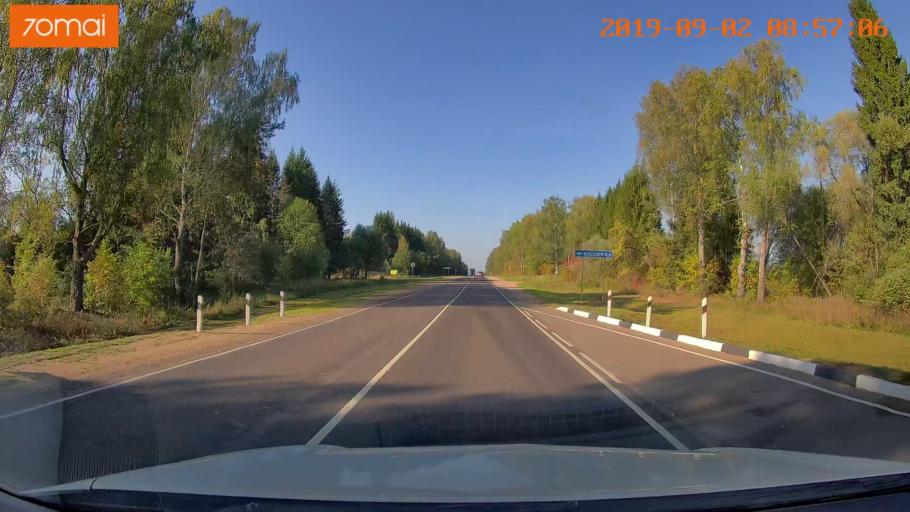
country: RU
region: Kaluga
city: Medyn'
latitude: 54.9397
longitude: 35.7765
